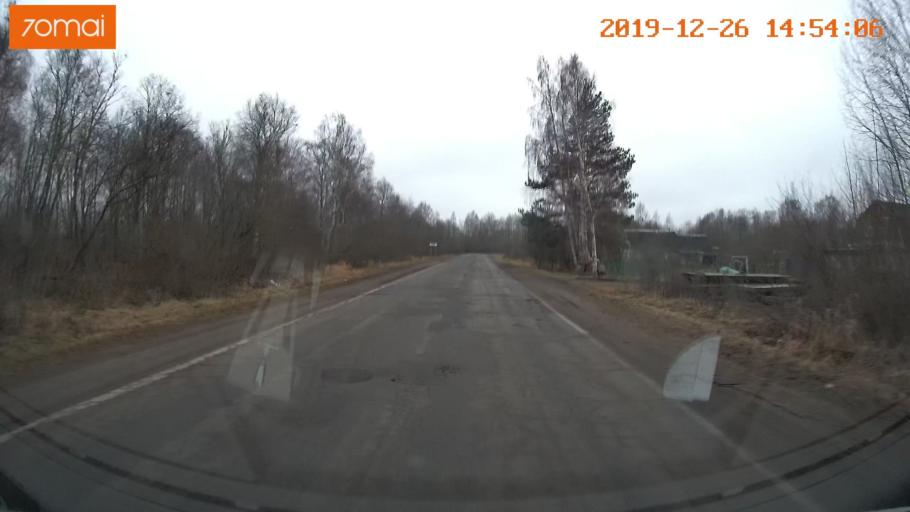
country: RU
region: Jaroslavl
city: Rybinsk
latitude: 58.3098
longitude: 38.8862
